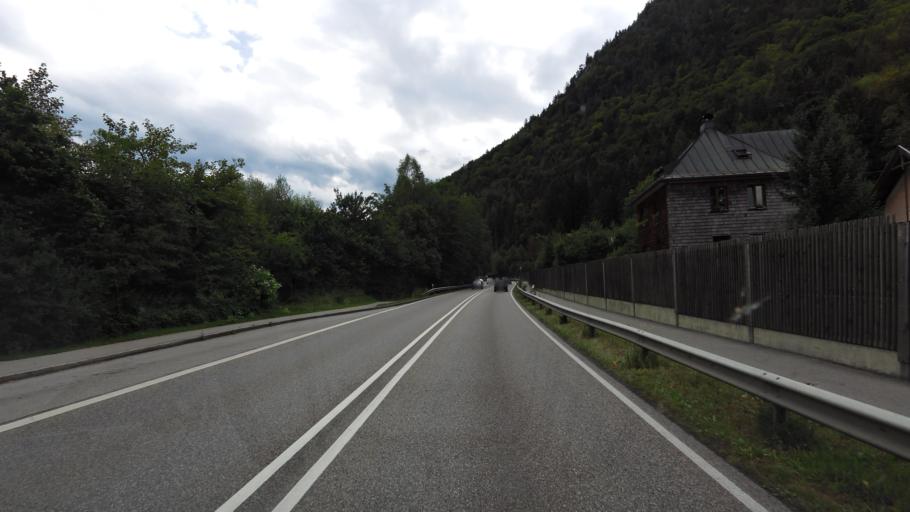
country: DE
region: Bavaria
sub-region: Upper Bavaria
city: Piding
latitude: 47.7569
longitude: 12.8992
